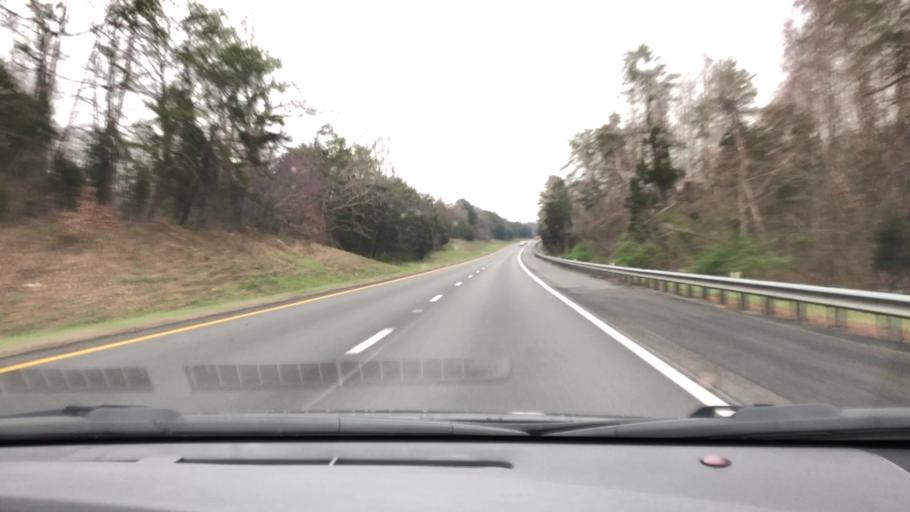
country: US
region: Virginia
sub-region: Fluvanna County
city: Lake Monticello
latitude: 37.9969
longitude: -78.2929
